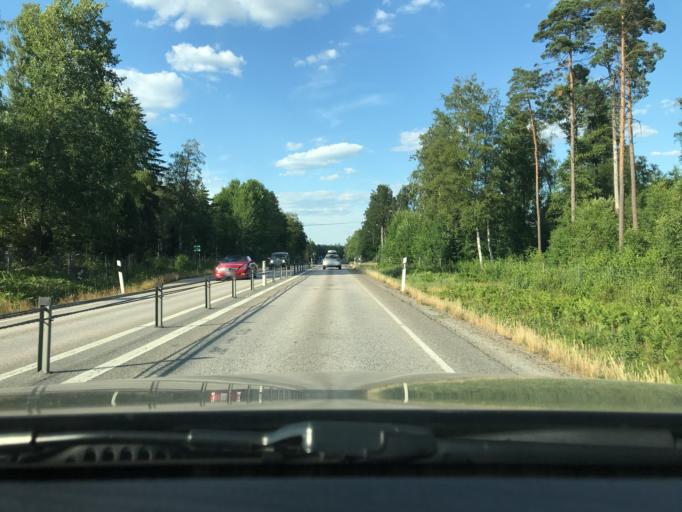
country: SE
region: Kronoberg
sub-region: Vaxjo Kommun
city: Rottne
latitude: 56.9870
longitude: 14.9910
